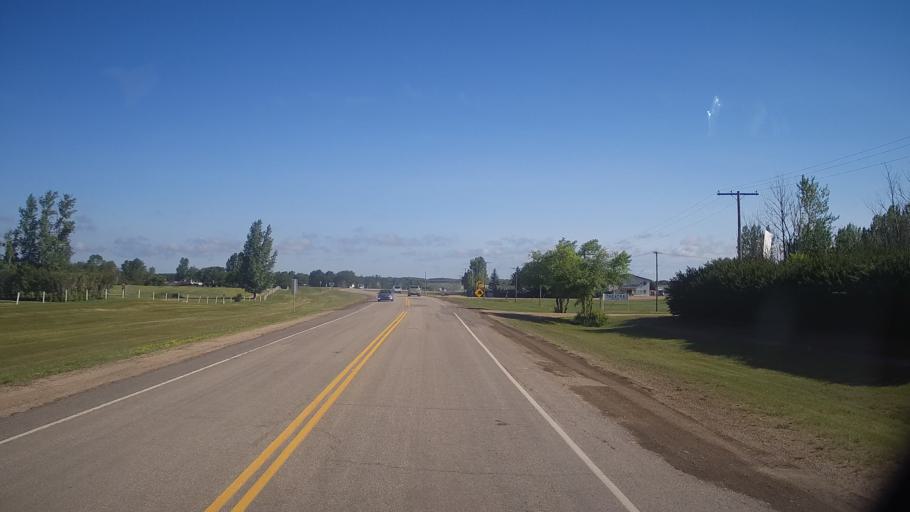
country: CA
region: Saskatchewan
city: Watrous
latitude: 51.7156
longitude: -105.4521
